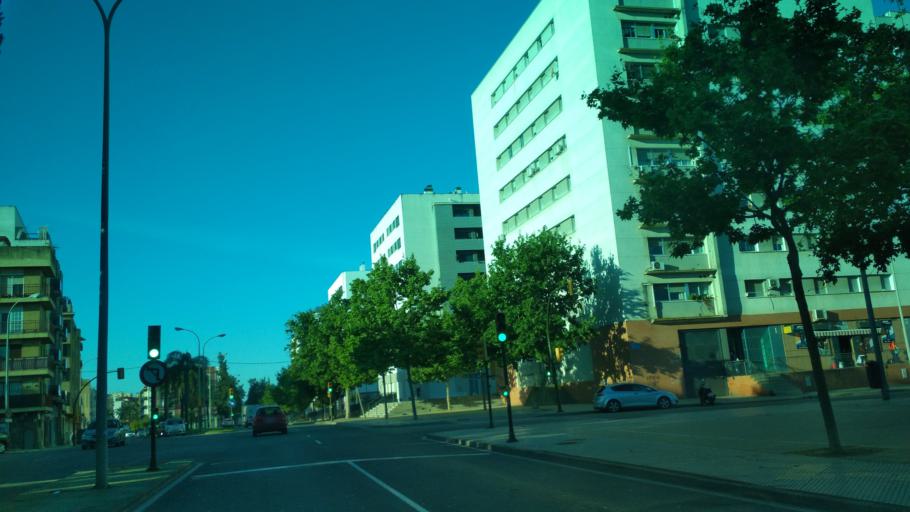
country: ES
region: Andalusia
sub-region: Provincia de Huelva
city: Huelva
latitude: 37.2758
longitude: -6.9492
